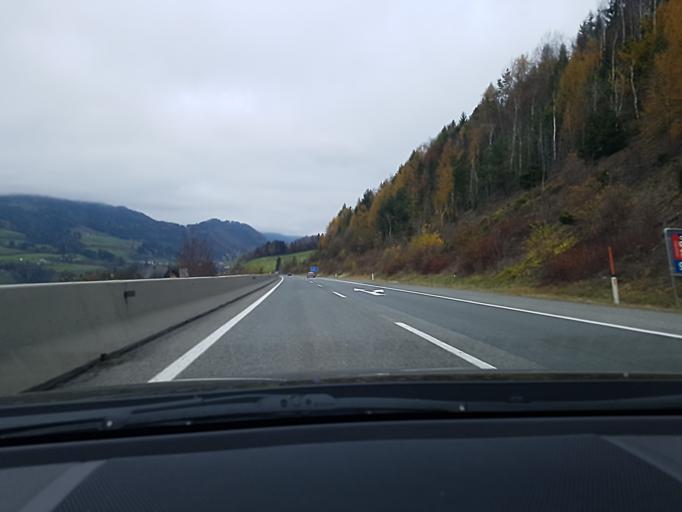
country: AT
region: Salzburg
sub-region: Politischer Bezirk Sankt Johann im Pongau
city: Pfarrwerfen
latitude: 47.4542
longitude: 13.2155
